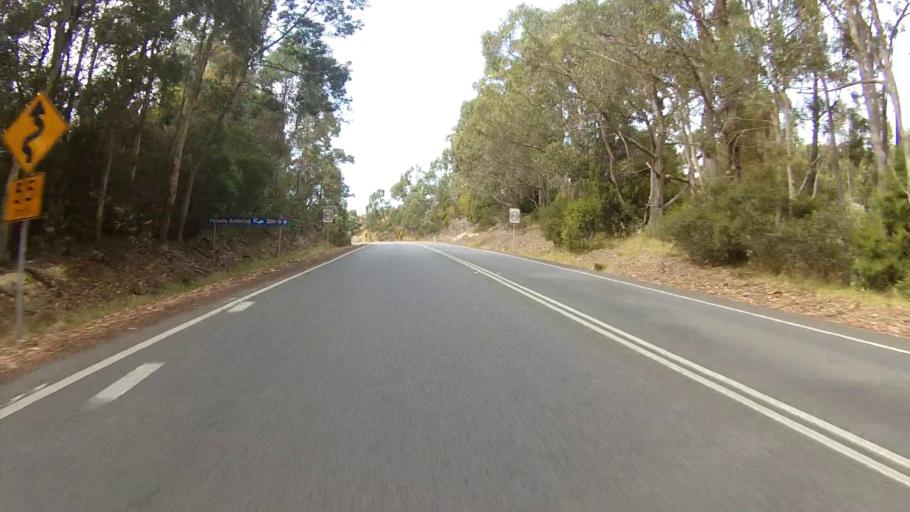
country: AU
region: Tasmania
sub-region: Kingborough
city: Kettering
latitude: -43.1112
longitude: 147.2423
